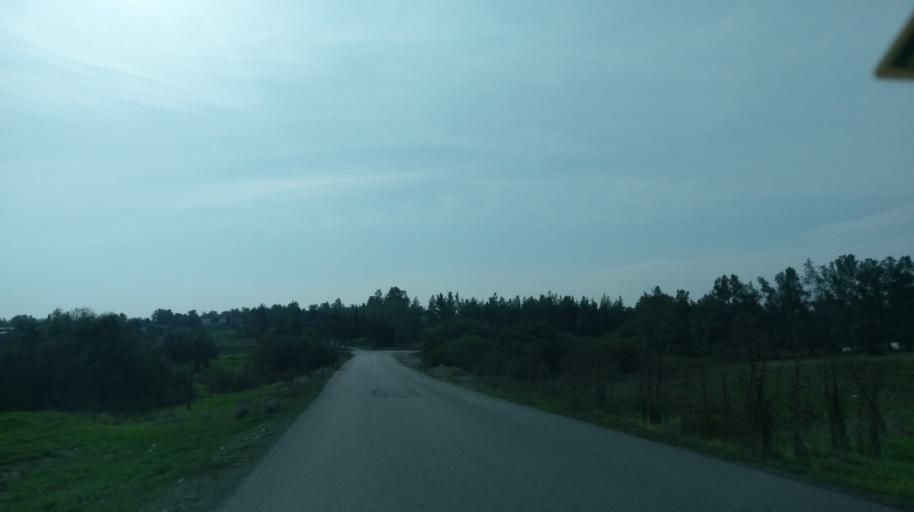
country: CY
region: Keryneia
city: Lapithos
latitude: 35.2741
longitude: 33.1228
